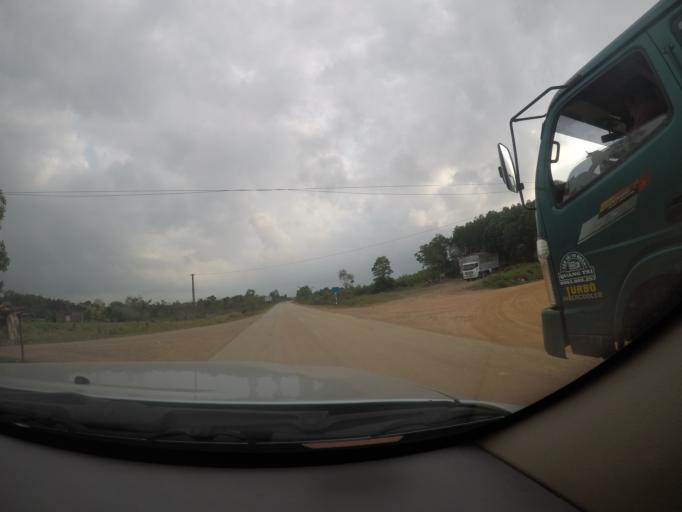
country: VN
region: Quang Tri
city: Ho Xa
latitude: 17.0771
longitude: 106.8618
